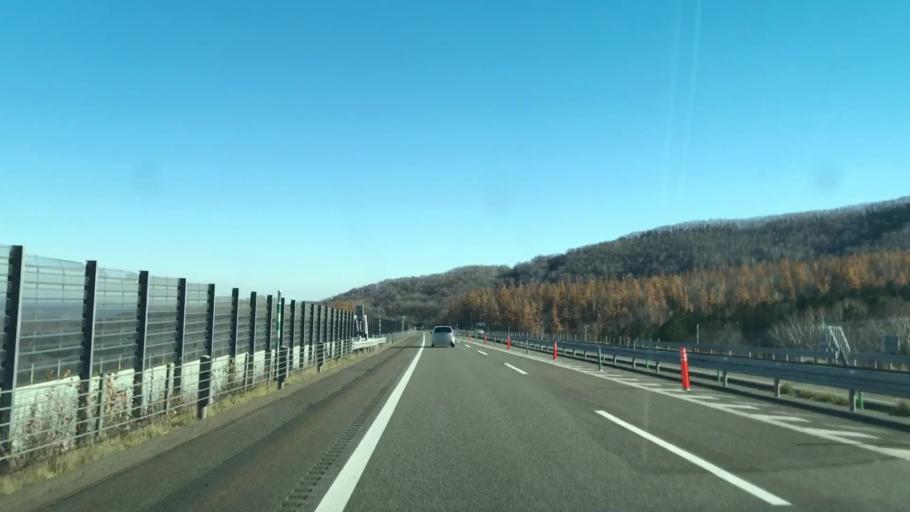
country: JP
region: Hokkaido
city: Otofuke
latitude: 43.0659
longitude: 142.7678
